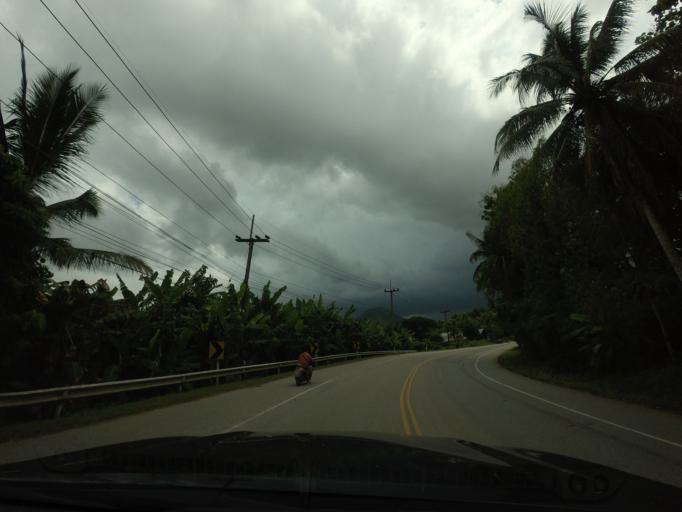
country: LA
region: Vientiane
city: Muang Sanakham
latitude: 17.9863
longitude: 101.7480
